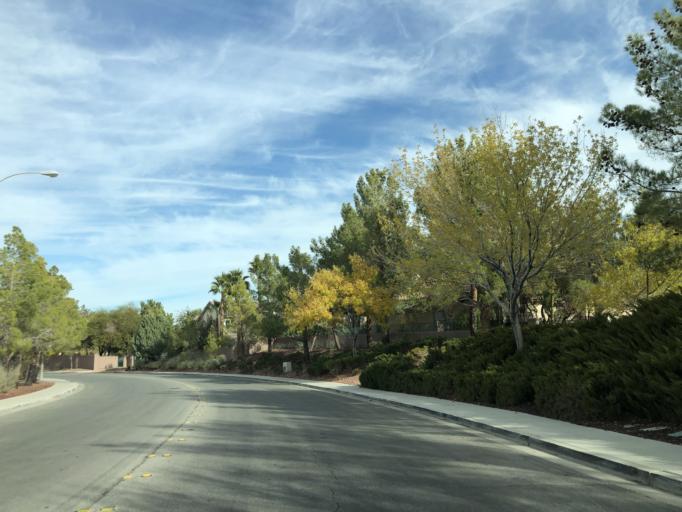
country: US
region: Nevada
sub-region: Clark County
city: Whitney
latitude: 36.0136
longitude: -115.0909
